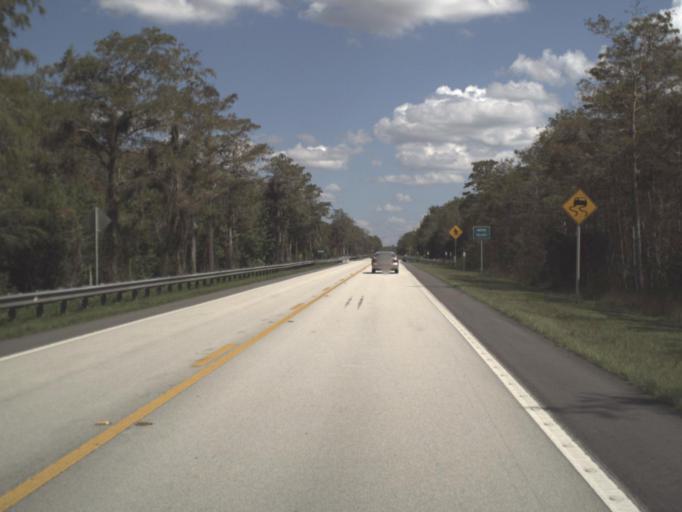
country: US
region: Florida
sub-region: Miami-Dade County
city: Kendall West
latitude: 25.8468
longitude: -80.9340
